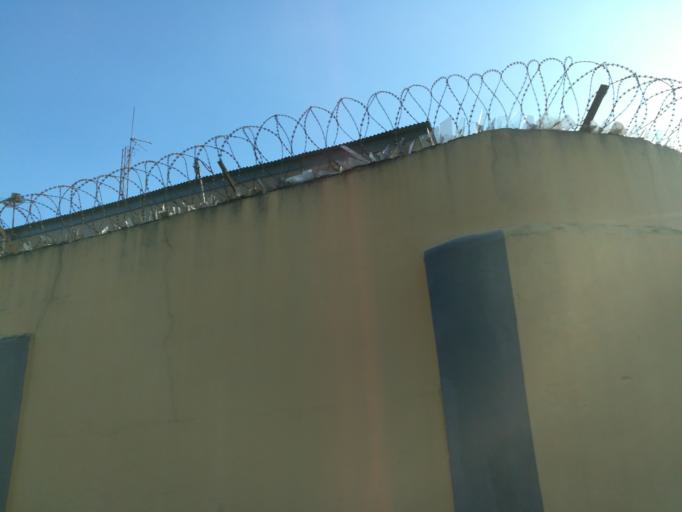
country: NG
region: Lagos
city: Ikeja
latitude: 6.6065
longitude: 3.3452
